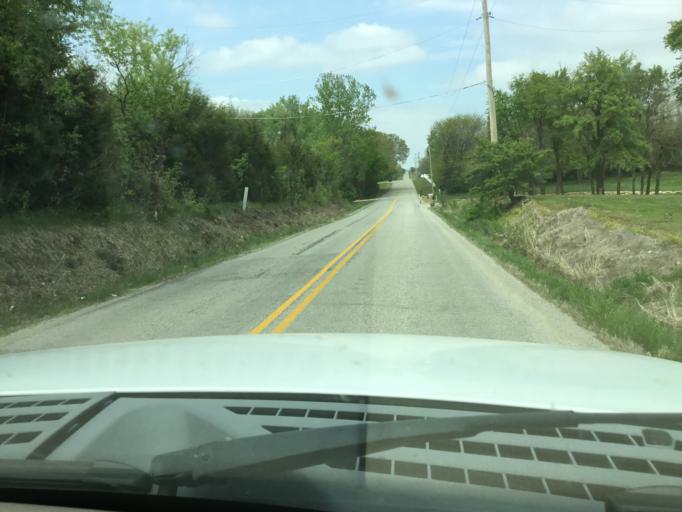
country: US
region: Kansas
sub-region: Shawnee County
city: Topeka
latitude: 38.9670
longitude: -95.6142
